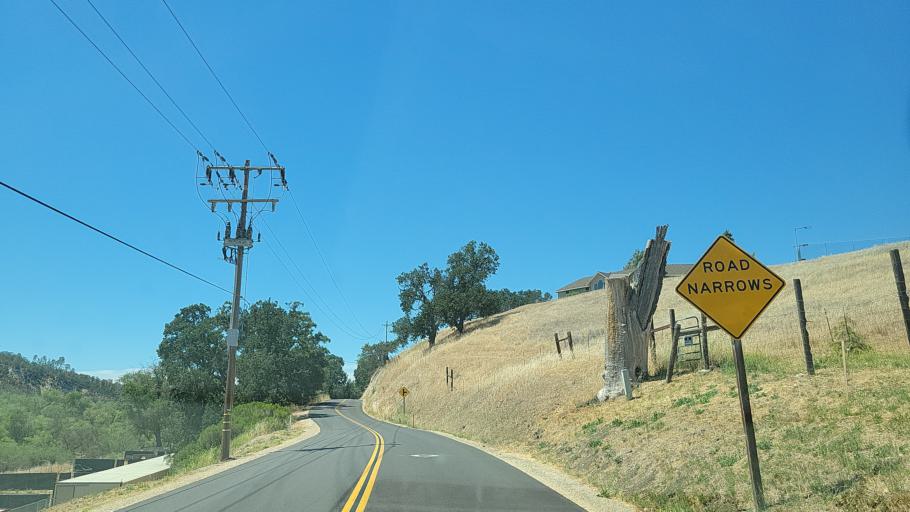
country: US
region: California
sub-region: San Luis Obispo County
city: Atascadero
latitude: 35.4891
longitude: -120.6386
